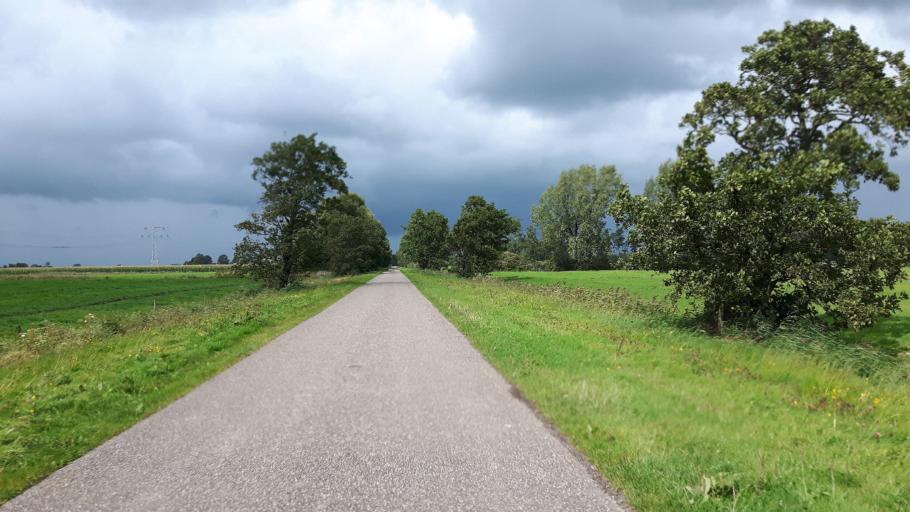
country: NL
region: Friesland
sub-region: Gemeente Dantumadiel
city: Broeksterwald
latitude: 53.2663
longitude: 5.9862
